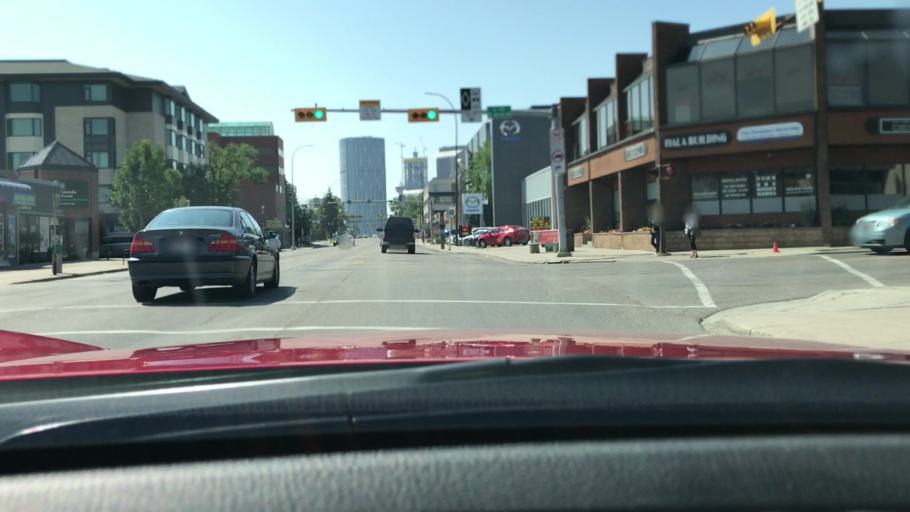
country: CA
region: Alberta
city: Calgary
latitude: 51.0635
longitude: -114.0626
